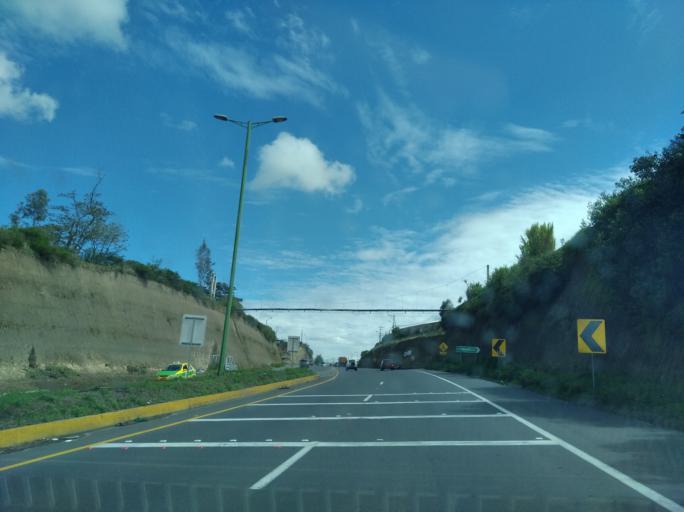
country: EC
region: Pichincha
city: Sangolqui
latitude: -0.1806
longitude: -78.3301
